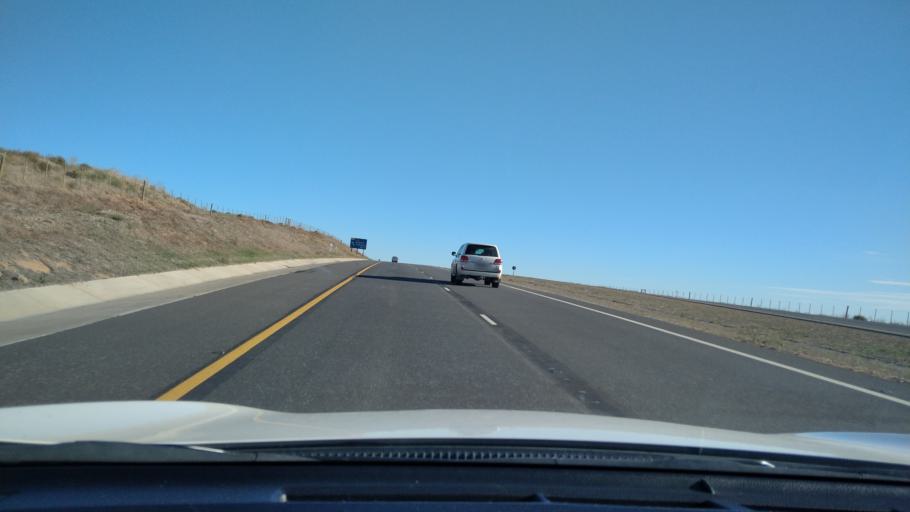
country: ZA
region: Western Cape
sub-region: West Coast District Municipality
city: Malmesbury
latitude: -33.4269
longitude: 18.7189
